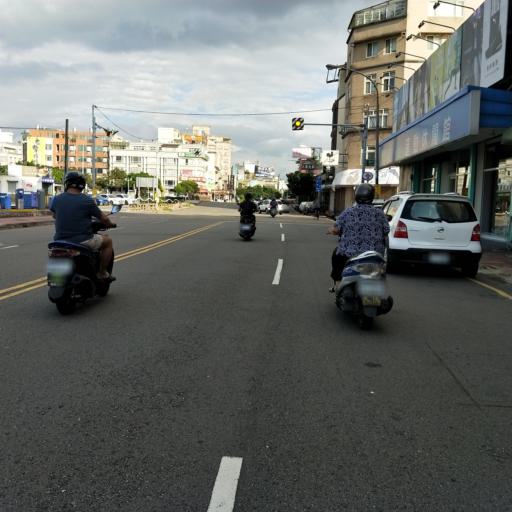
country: TW
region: Taiwan
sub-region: Hsinchu
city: Zhubei
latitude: 24.8326
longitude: 121.0081
